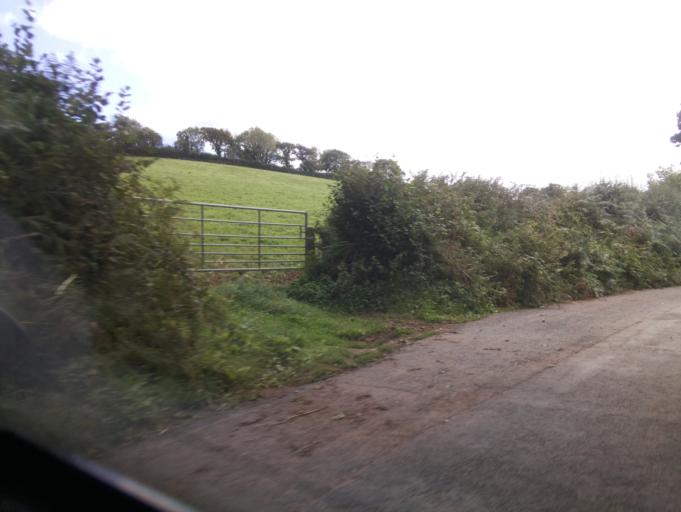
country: GB
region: England
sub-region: Devon
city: Totnes
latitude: 50.4009
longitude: -3.7110
